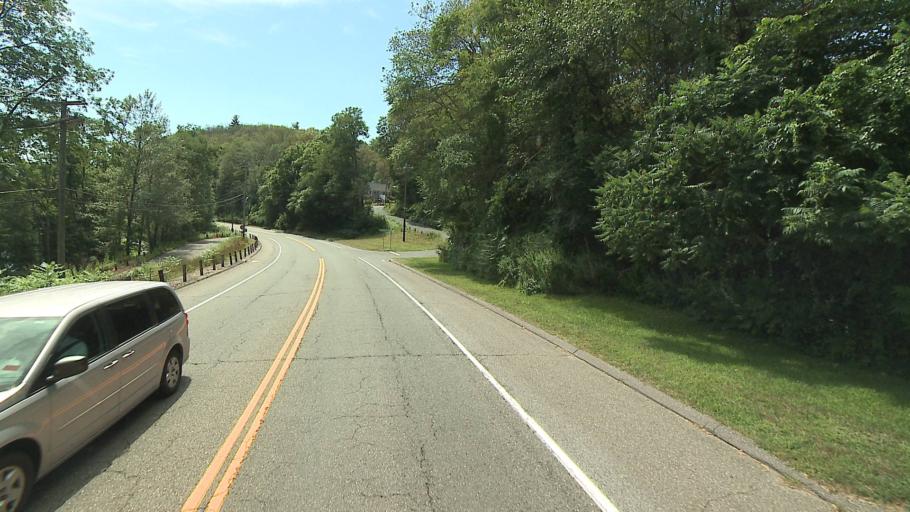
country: US
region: Connecticut
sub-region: Hartford County
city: Collinsville
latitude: 41.8030
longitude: -72.9285
